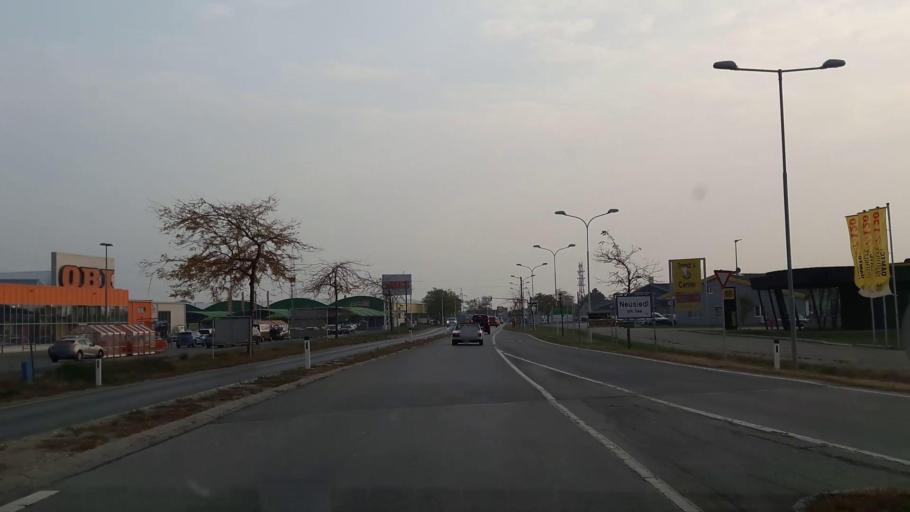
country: AT
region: Burgenland
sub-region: Politischer Bezirk Neusiedl am See
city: Neusiedl am See
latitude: 47.9701
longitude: 16.8381
